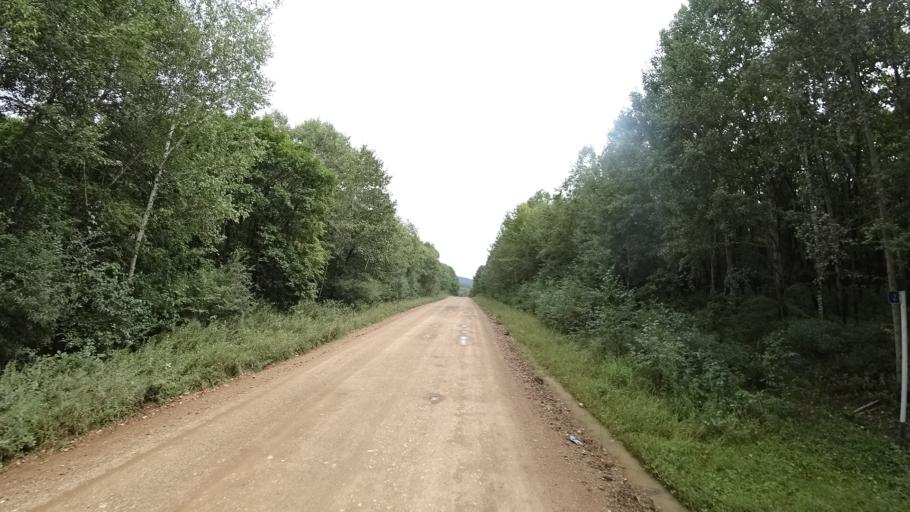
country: RU
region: Primorskiy
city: Lyalichi
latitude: 44.0859
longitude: 132.4405
